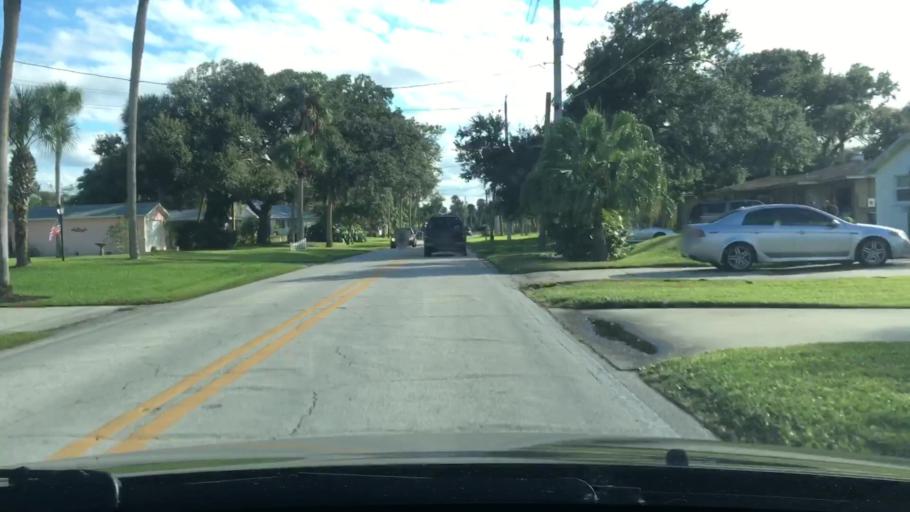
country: US
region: Florida
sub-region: Volusia County
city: Ormond-by-the-Sea
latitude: 29.3266
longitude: -81.0644
